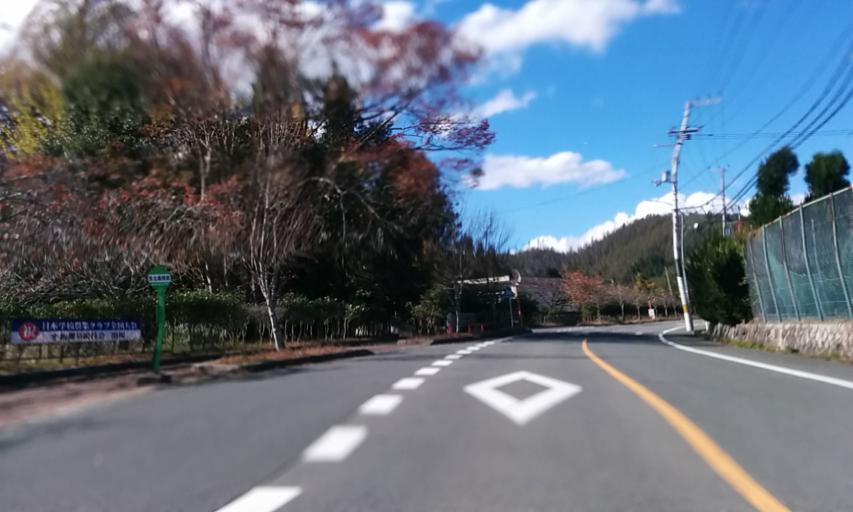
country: JP
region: Kyoto
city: Kameoka
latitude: 35.1972
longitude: 135.6341
